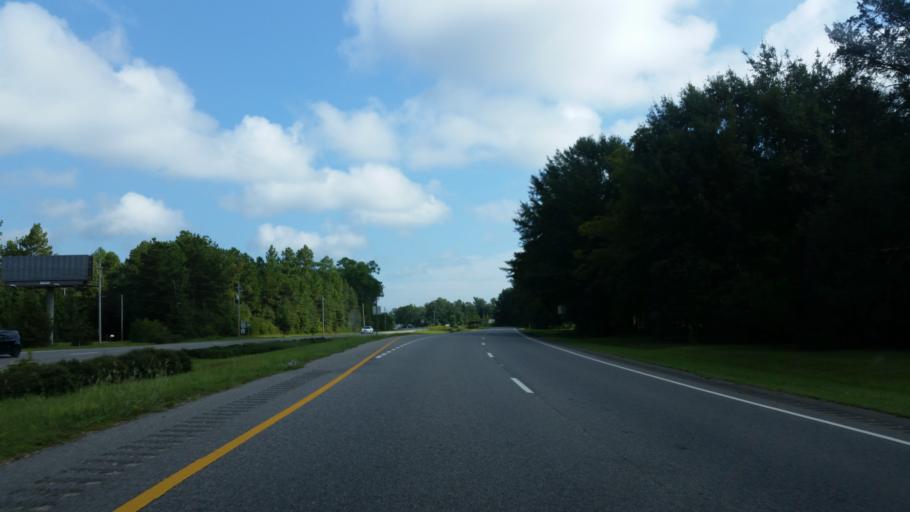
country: US
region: Alabama
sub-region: Baldwin County
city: Bay Minette
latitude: 30.9362
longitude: -87.7682
